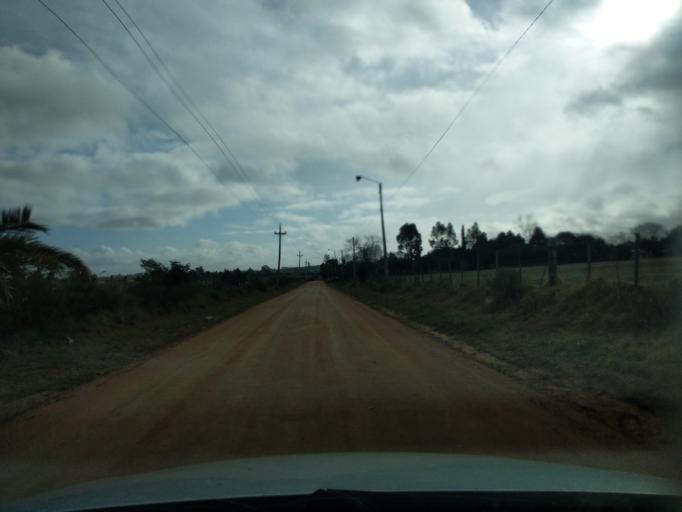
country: UY
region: Florida
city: Florida
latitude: -34.0715
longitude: -56.2207
